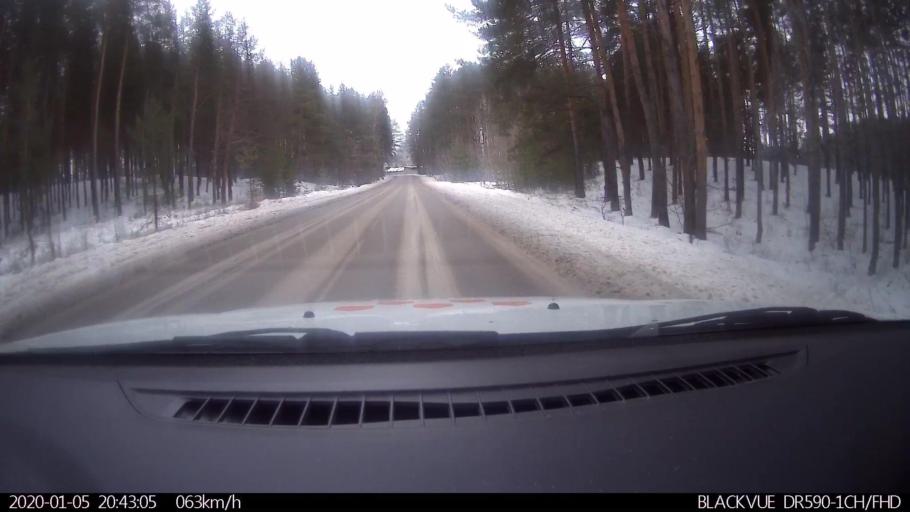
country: RU
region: Nizjnij Novgorod
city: Lukino
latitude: 56.3926
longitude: 43.7371
